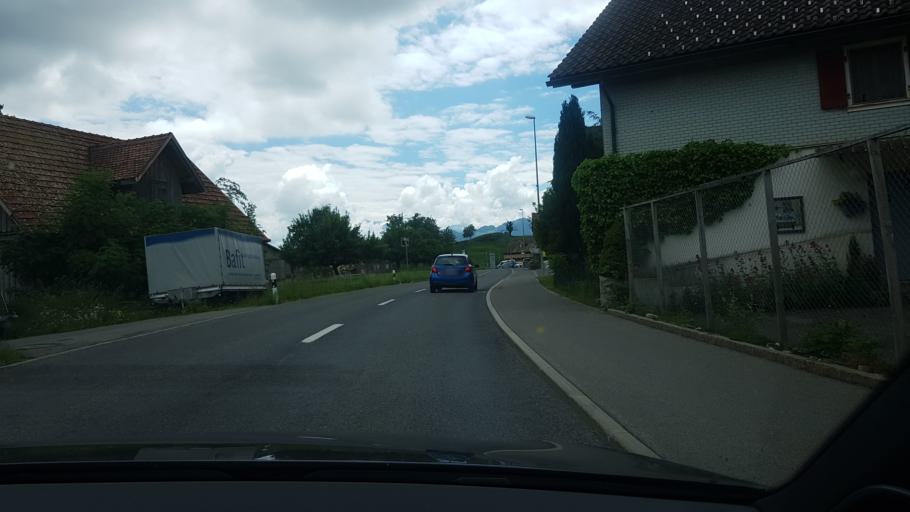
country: CH
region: Schwyz
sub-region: Bezirk Schwyz
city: Sattel
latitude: 47.0843
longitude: 8.6292
